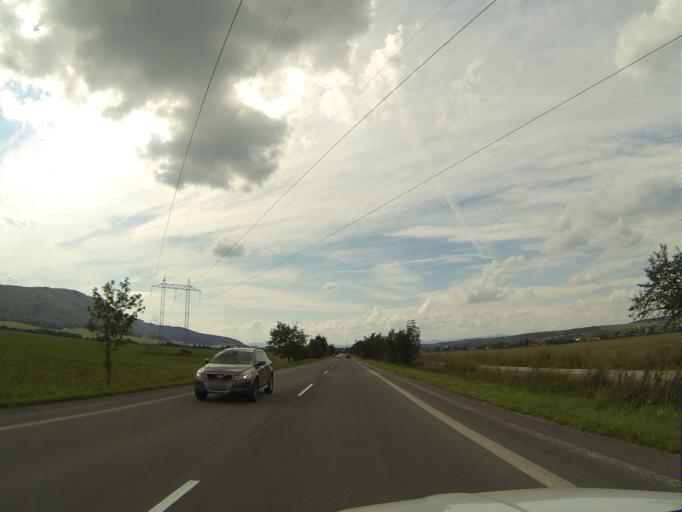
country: SK
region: Nitriansky
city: Partizanske
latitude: 48.6254
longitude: 18.4428
